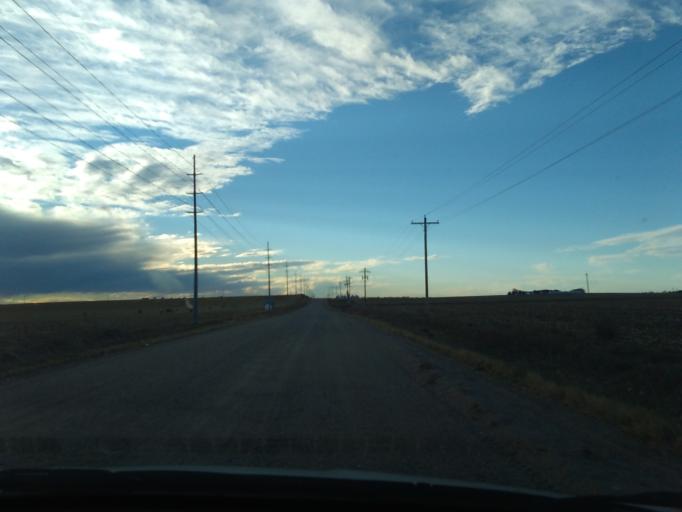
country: US
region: Nebraska
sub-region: Phelps County
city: Holdrege
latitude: 40.4088
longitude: -99.3622
